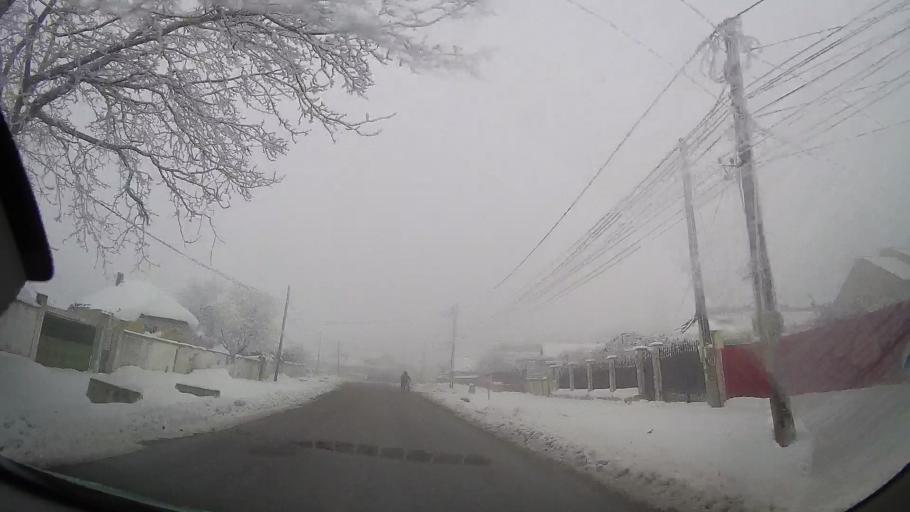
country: RO
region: Neamt
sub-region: Comuna Sabaoani
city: Sabaoani
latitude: 47.0139
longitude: 26.8627
